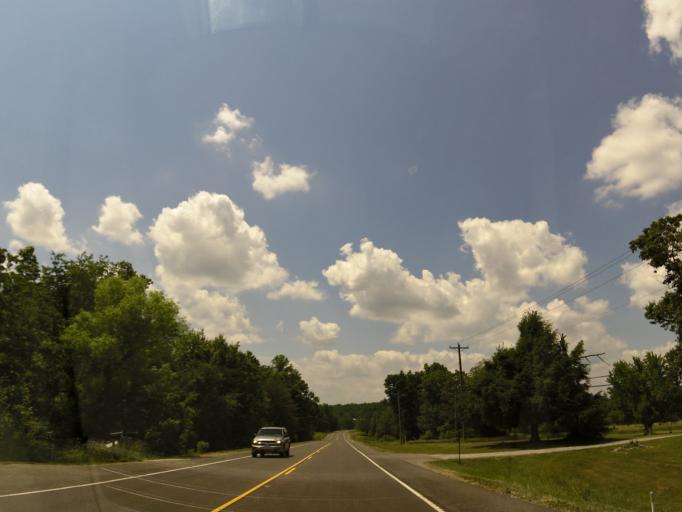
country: US
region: Tennessee
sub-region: Rhea County
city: Dayton
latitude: 35.5550
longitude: -85.0880
